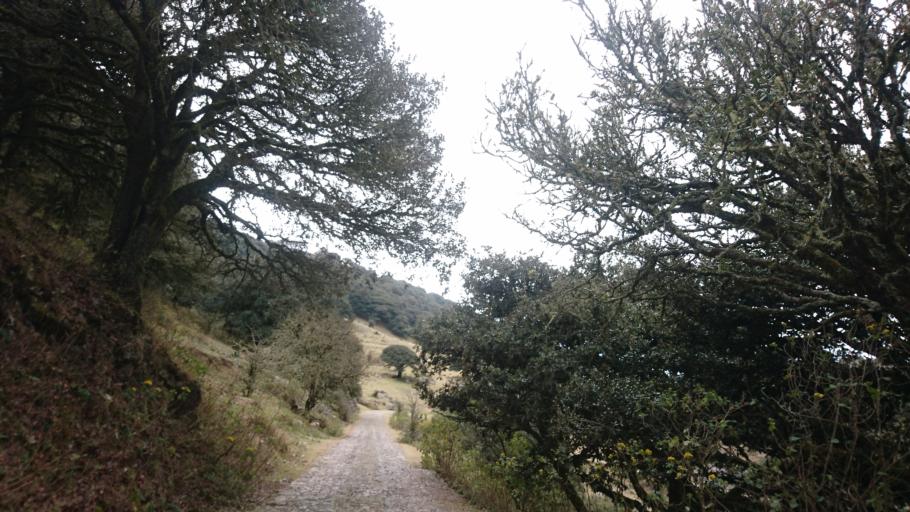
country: MX
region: San Luis Potosi
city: Zaragoza
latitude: 22.0690
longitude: -100.6408
